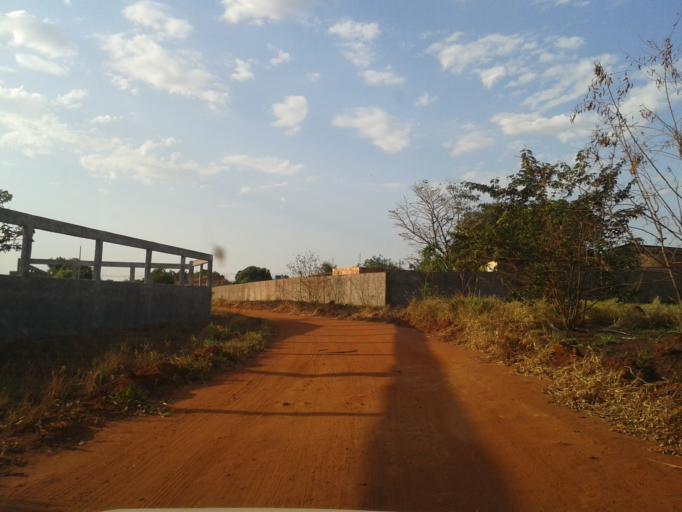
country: BR
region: Minas Gerais
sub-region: Ituiutaba
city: Ituiutaba
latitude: -18.9975
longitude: -49.4369
